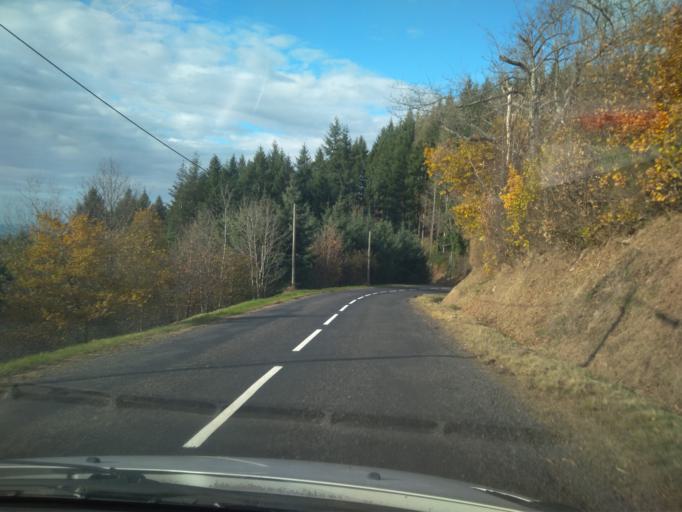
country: FR
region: Auvergne
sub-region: Departement de l'Allier
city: Le Mayet-de-Montagne
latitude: 46.1419
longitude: 3.7497
